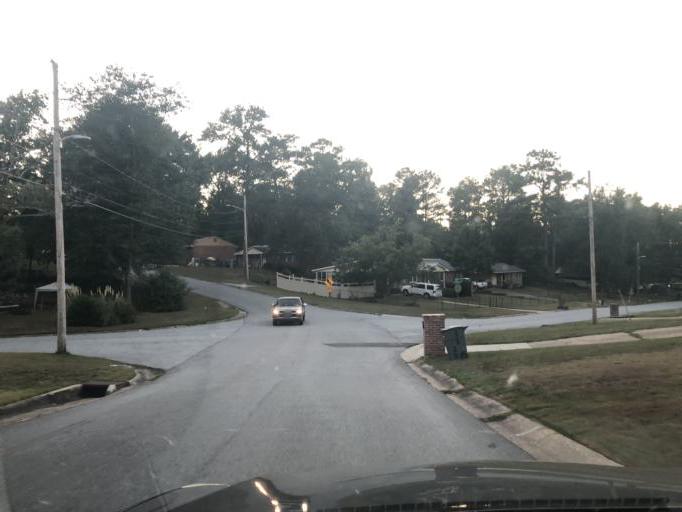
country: US
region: Georgia
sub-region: Muscogee County
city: Columbus
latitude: 32.4672
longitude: -84.8976
